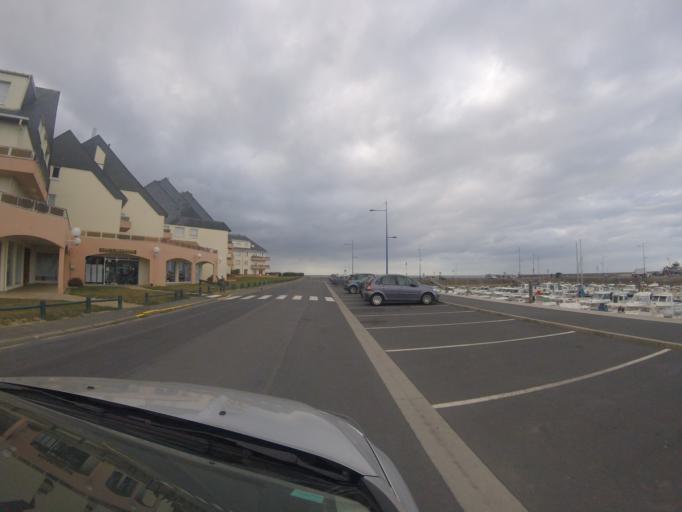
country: FR
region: Lower Normandy
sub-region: Departement du Calvados
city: Grandcamp-Maisy
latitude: 49.3884
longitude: -1.0506
